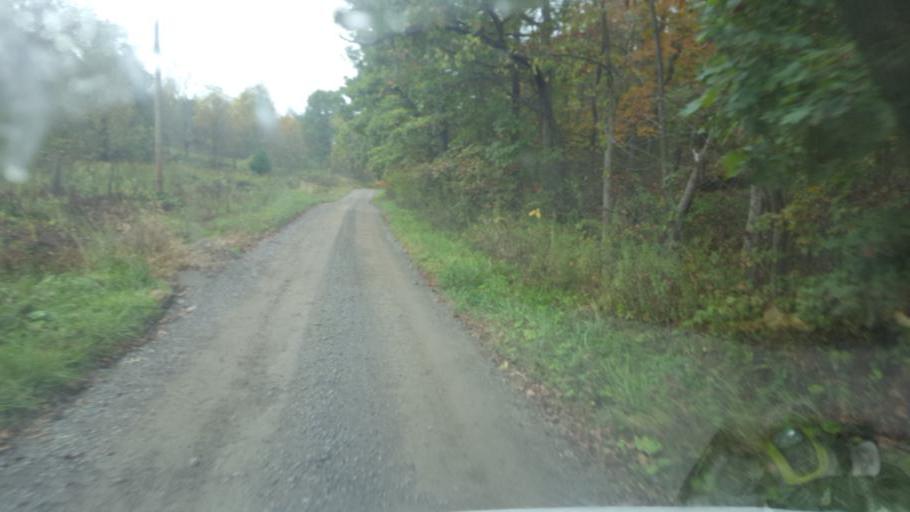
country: US
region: Ohio
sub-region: Holmes County
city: Millersburg
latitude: 40.5357
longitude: -82.0411
